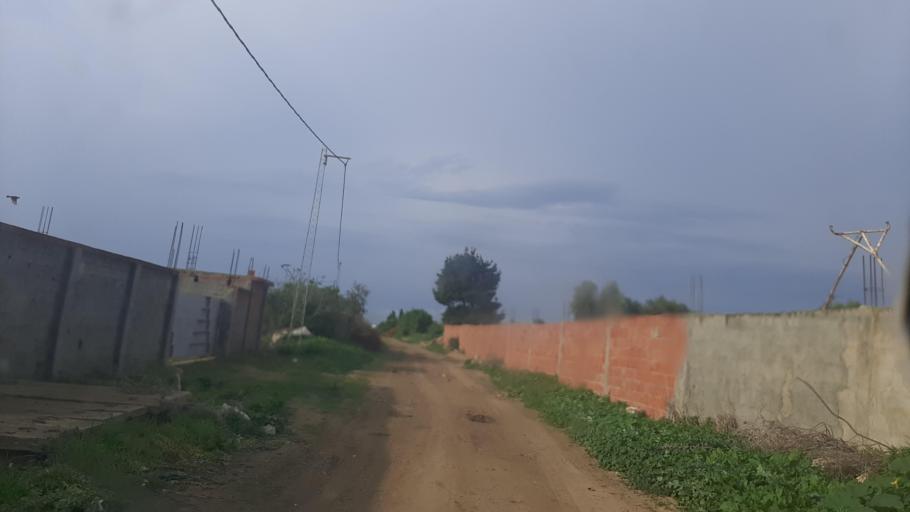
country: TN
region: Nabul
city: Menzel Heurr
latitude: 36.7903
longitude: 10.9613
